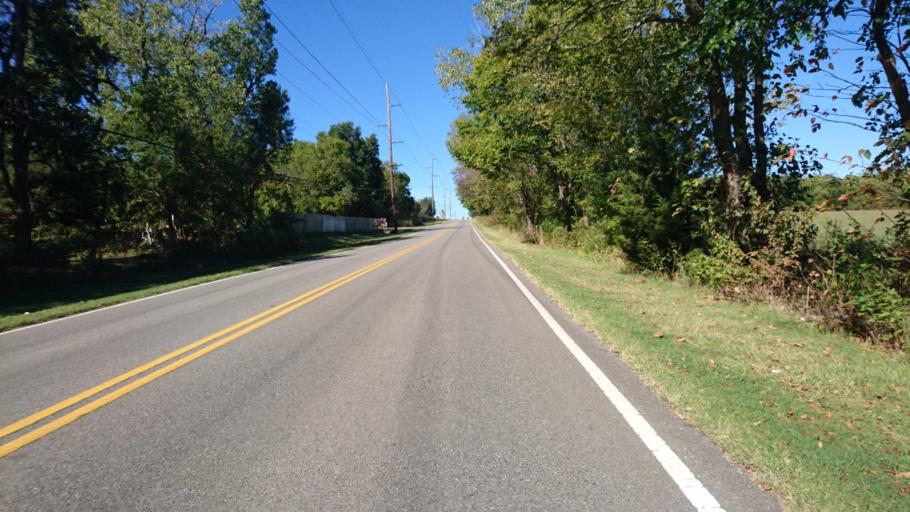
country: US
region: Oklahoma
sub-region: Rogers County
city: Catoosa
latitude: 36.1480
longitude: -95.7994
